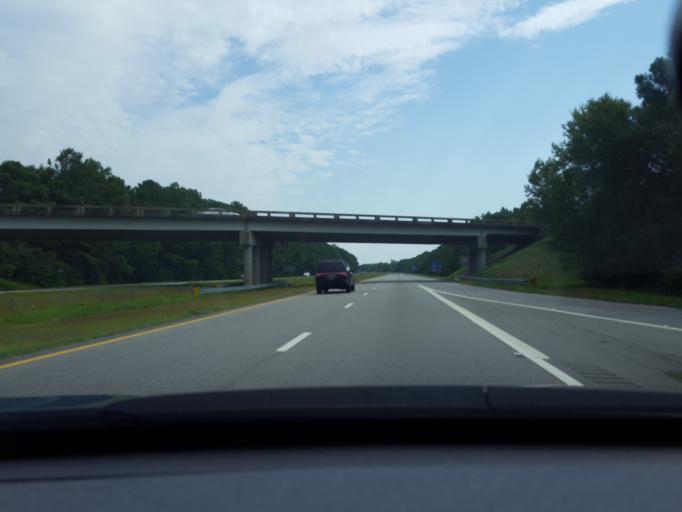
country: US
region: North Carolina
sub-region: Chowan County
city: Edenton
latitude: 36.0695
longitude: -76.6311
